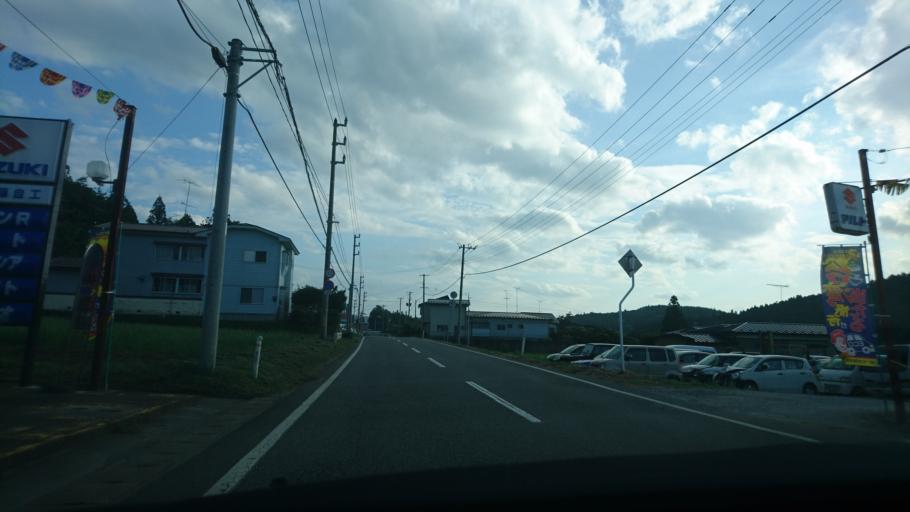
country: JP
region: Iwate
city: Mizusawa
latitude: 39.0313
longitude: 141.2952
